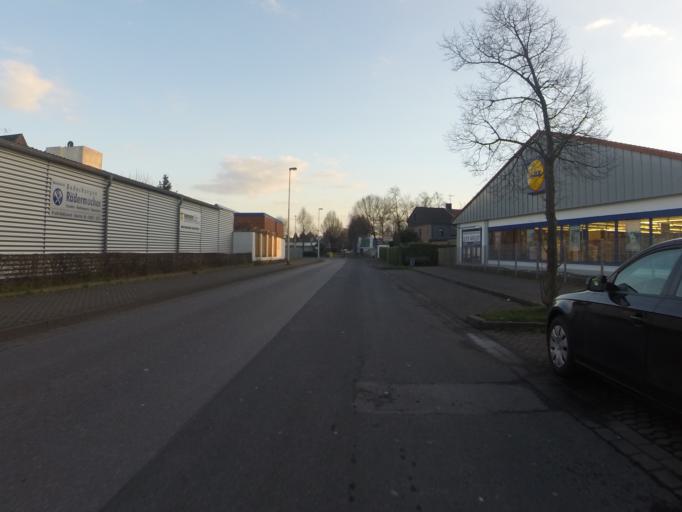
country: NL
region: Limburg
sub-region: Gemeente Kerkrade
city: Kerkrade
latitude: 50.8328
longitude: 6.0845
